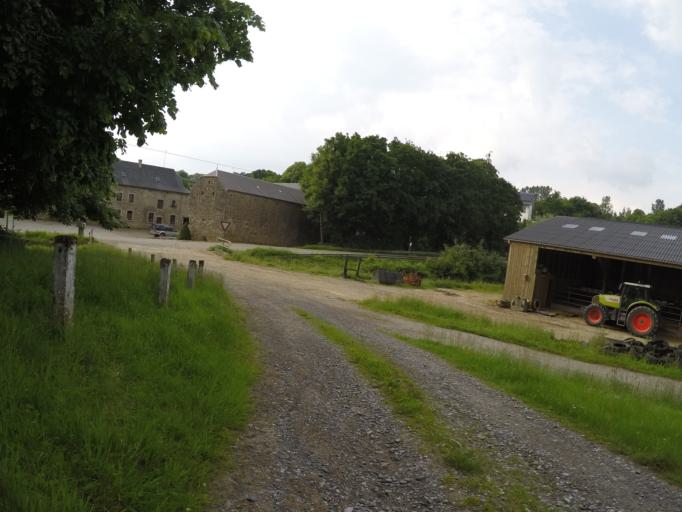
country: BE
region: Wallonia
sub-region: Province de Namur
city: Assesse
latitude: 50.3171
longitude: 5.0246
